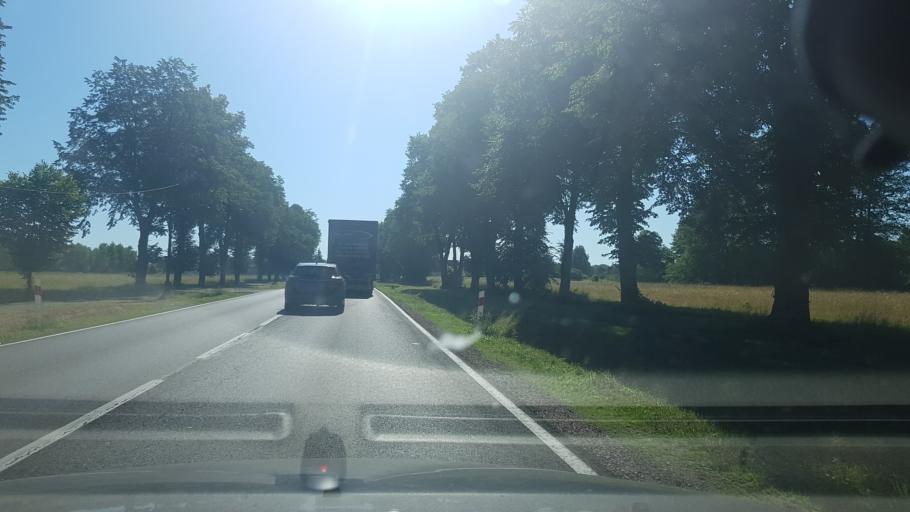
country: PL
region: Masovian Voivodeship
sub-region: Powiat wegrowski
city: Lochow
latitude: 52.5400
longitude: 21.6554
